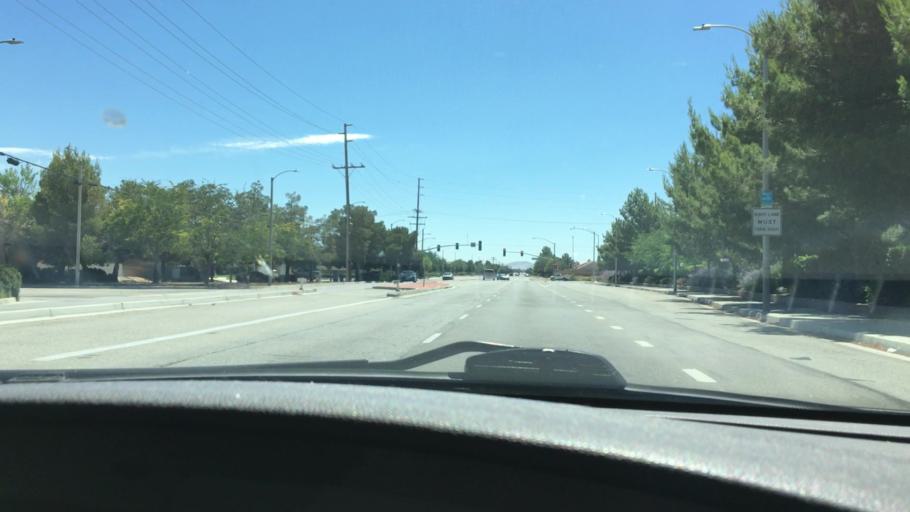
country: US
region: California
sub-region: Los Angeles County
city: Lancaster
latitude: 34.6750
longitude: -118.0967
